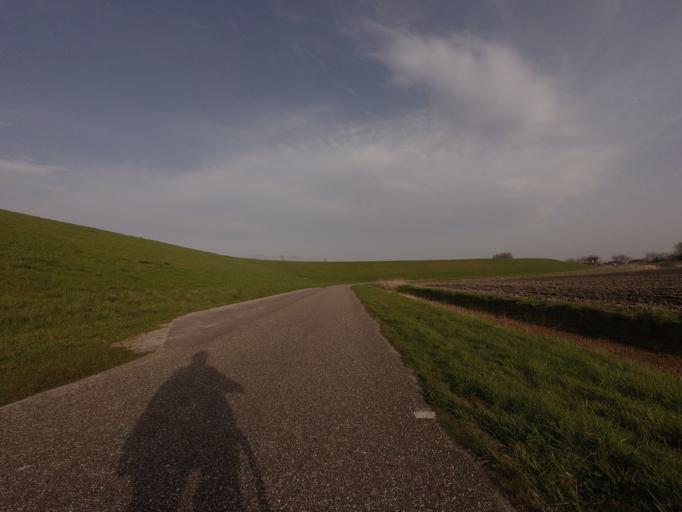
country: NL
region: Zeeland
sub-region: Gemeente Reimerswaal
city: Yerseke
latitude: 51.4053
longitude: 3.9910
